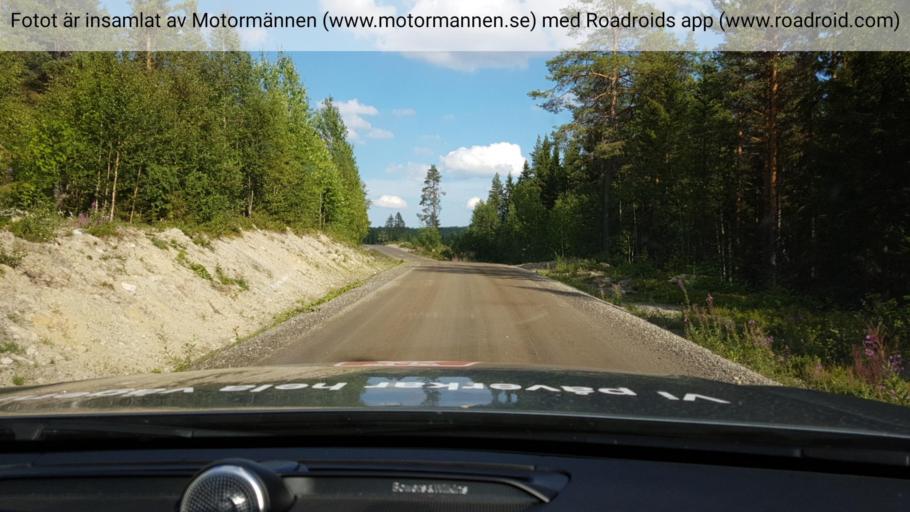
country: SE
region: Vaesterbotten
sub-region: Dorotea Kommun
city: Dorotea
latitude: 63.9290
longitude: 16.1227
